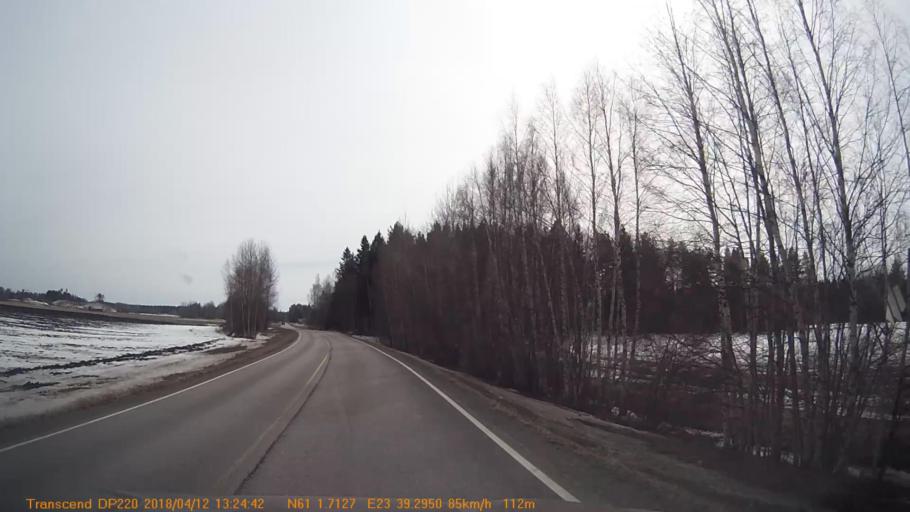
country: FI
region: Pirkanmaa
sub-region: Etelae-Pirkanmaa
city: Kylmaekoski
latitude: 61.0275
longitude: 23.6555
